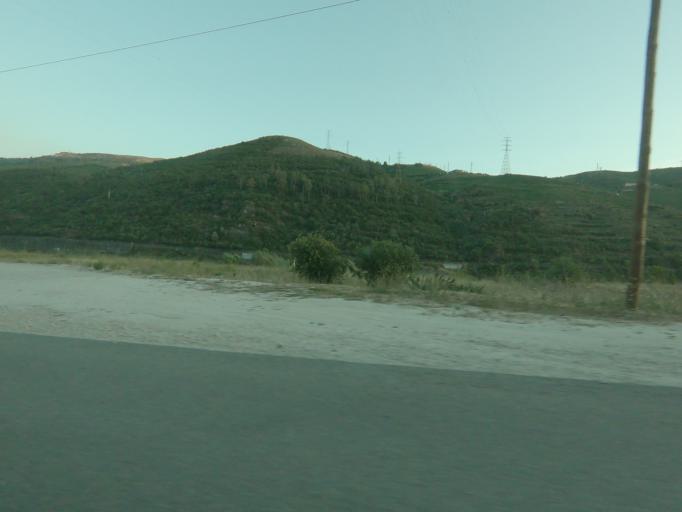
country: PT
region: Vila Real
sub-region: Peso da Regua
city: Peso da Regua
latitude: 41.1506
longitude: -7.7487
